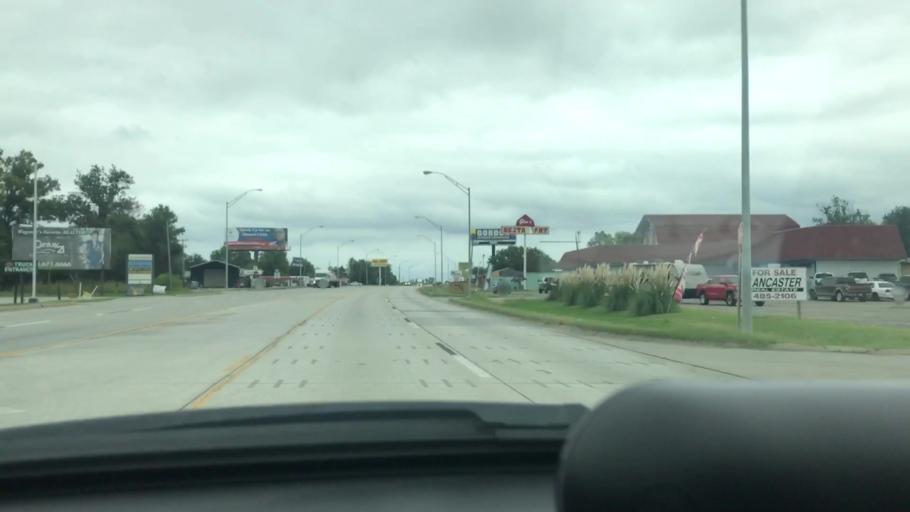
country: US
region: Oklahoma
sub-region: Wagoner County
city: Wagoner
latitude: 35.9619
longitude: -95.3938
